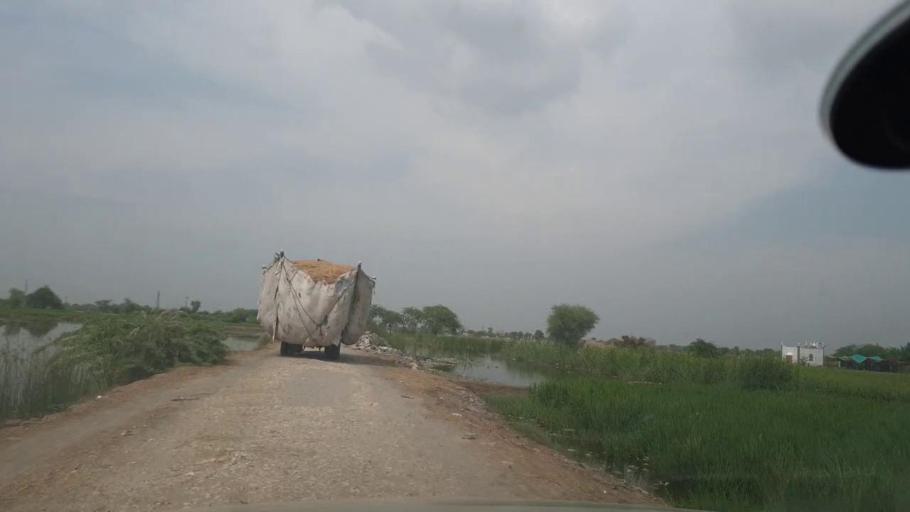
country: PK
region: Sindh
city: Jacobabad
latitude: 28.2564
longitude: 68.4371
